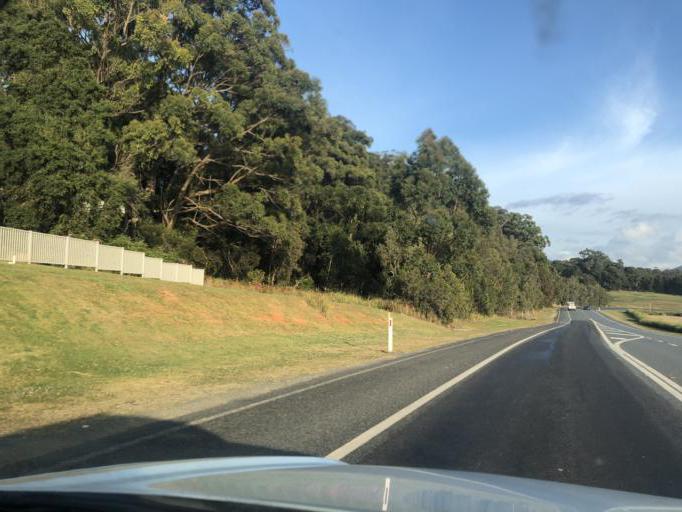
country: AU
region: New South Wales
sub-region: Coffs Harbour
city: Boambee
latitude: -30.3236
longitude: 153.0902
